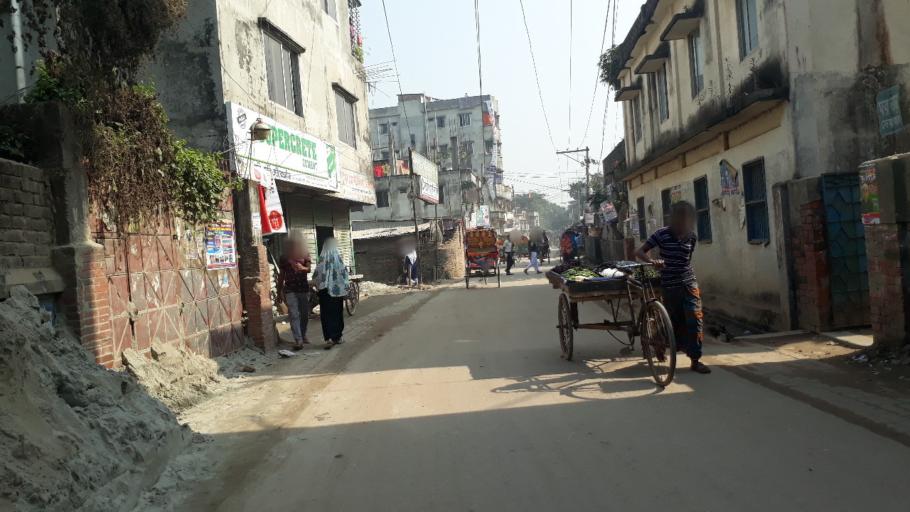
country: BD
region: Dhaka
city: Tungi
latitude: 23.8524
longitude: 90.2507
